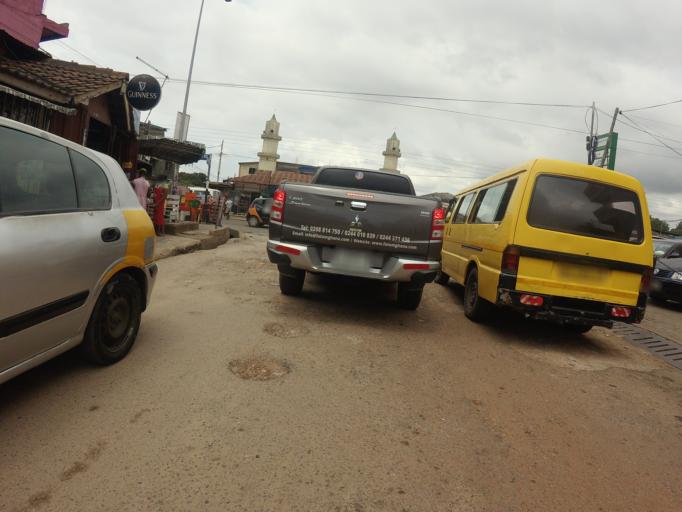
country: GH
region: Greater Accra
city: Accra
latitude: 5.5820
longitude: -0.2085
